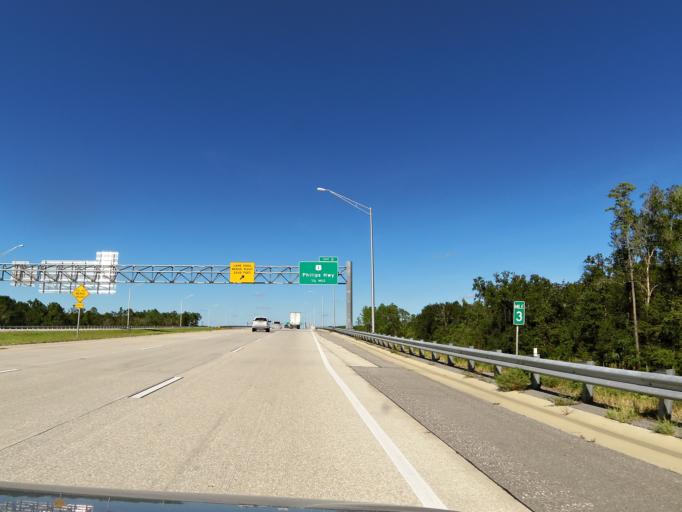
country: US
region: Florida
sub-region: Saint Johns County
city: Palm Valley
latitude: 30.1308
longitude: -81.5101
